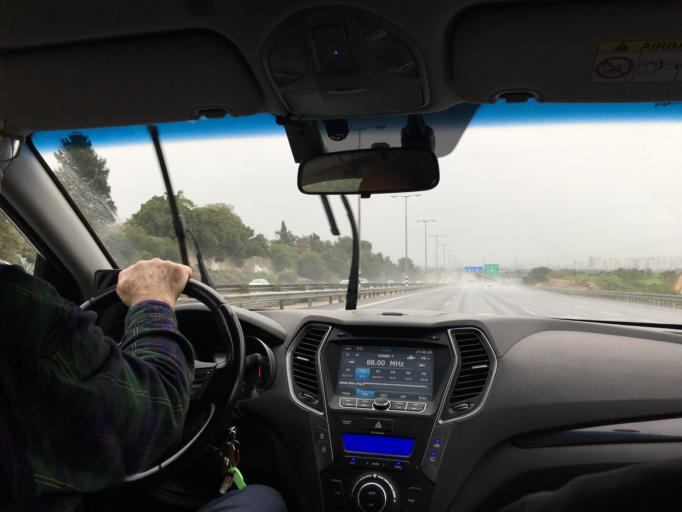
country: IL
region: Tel Aviv
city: Ramat HaSharon
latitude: 32.1284
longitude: 34.8469
